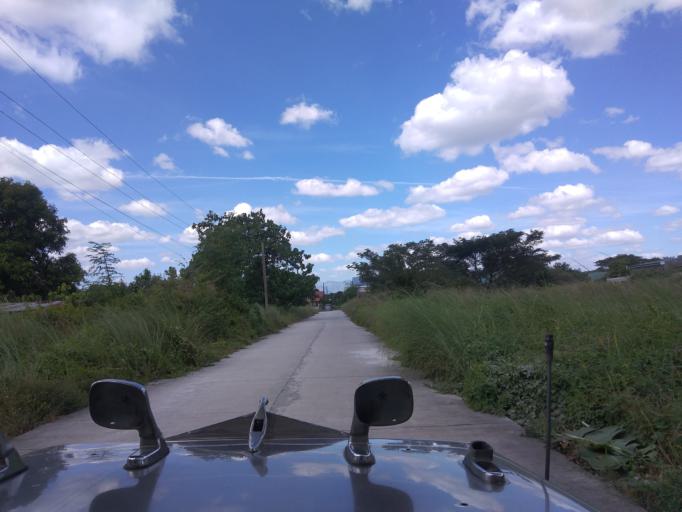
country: PH
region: Central Luzon
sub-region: Province of Pampanga
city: Santa Rita
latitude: 15.0085
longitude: 120.5920
